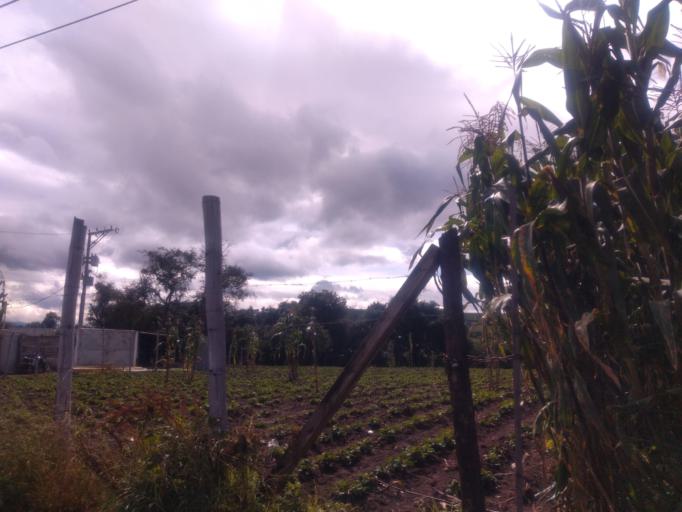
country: GT
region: Quetzaltenango
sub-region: Municipio de La Esperanza
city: La Esperanza
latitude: 14.8547
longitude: -91.5652
